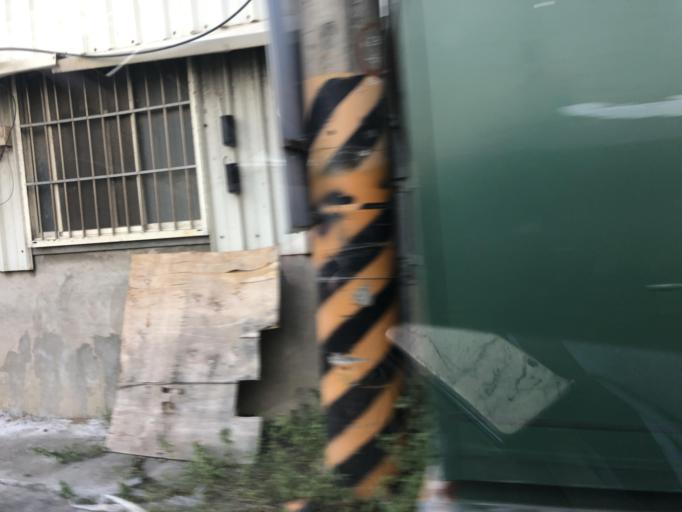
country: TW
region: Taiwan
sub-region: Tainan
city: Tainan
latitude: 23.0435
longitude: 120.2474
